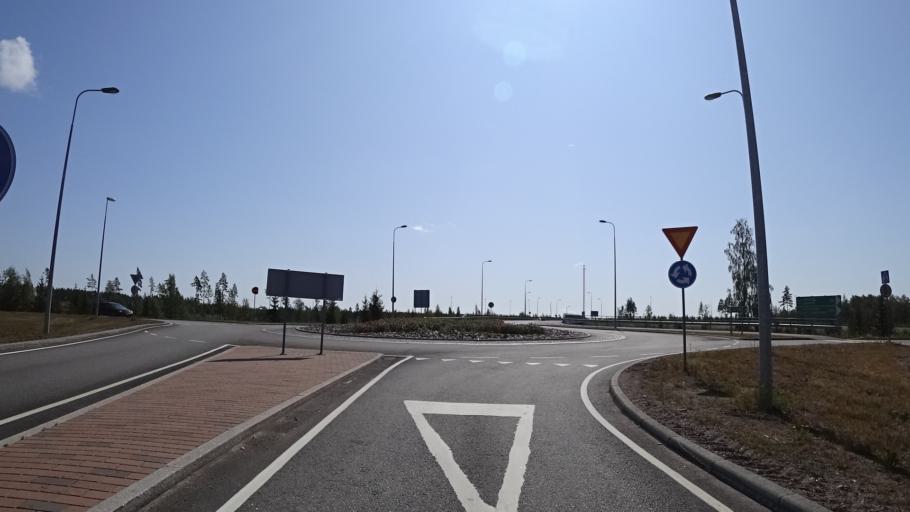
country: FI
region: Kymenlaakso
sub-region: Kotka-Hamina
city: Pyhtaeae
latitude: 60.4888
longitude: 26.5632
